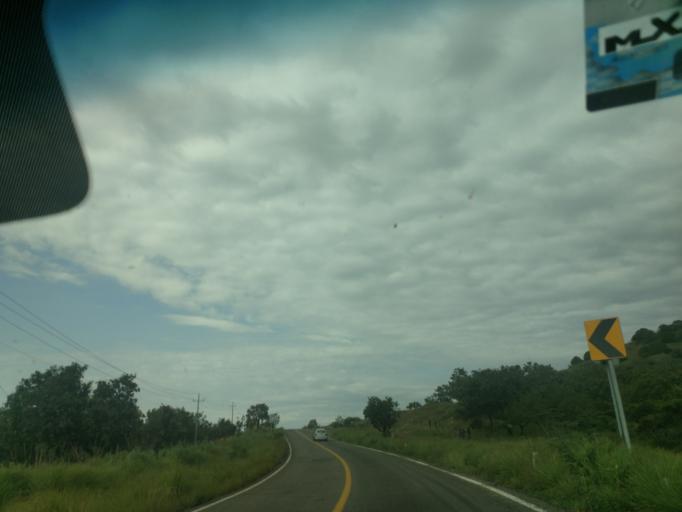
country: MX
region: Jalisco
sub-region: Atengo
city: Soyatlan del Oro
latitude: 20.5501
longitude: -104.3016
